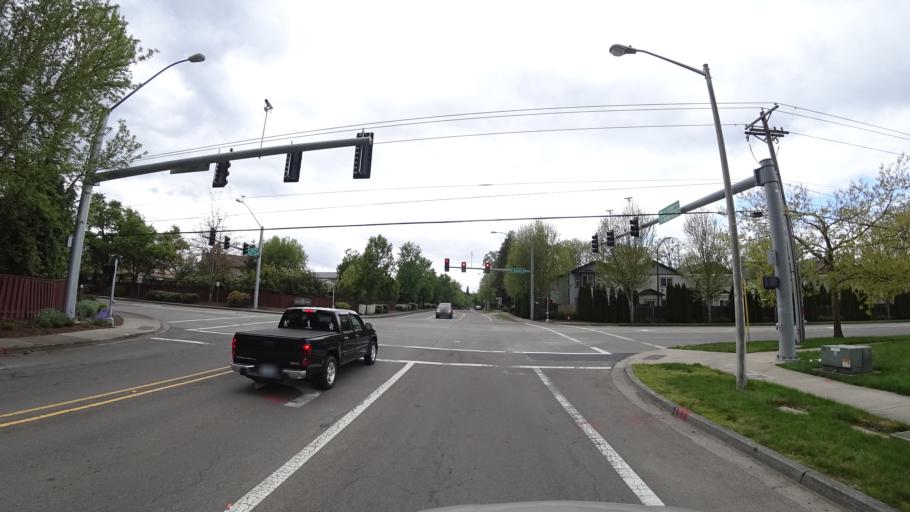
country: US
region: Oregon
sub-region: Washington County
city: Rockcreek
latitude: 45.5381
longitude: -122.9258
